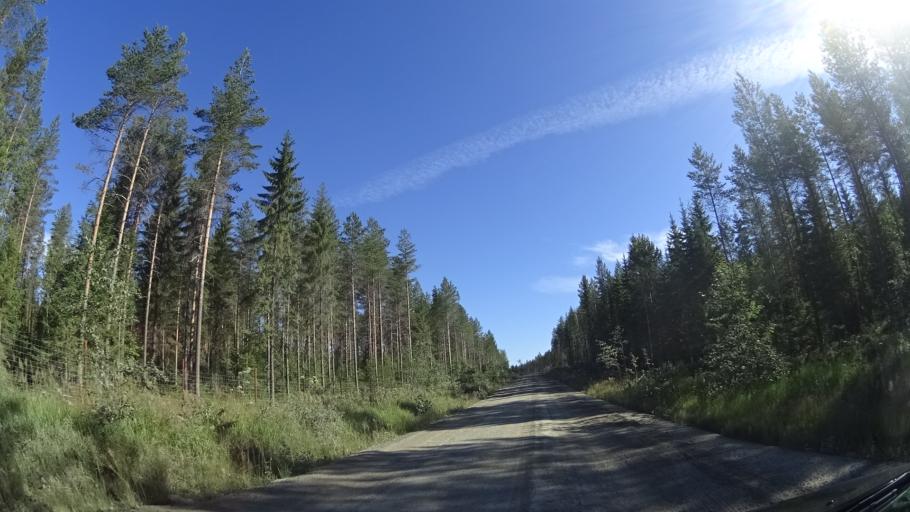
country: FI
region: Central Finland
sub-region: Jyvaeskylae
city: Petaejaevesi
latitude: 62.3076
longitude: 25.3409
